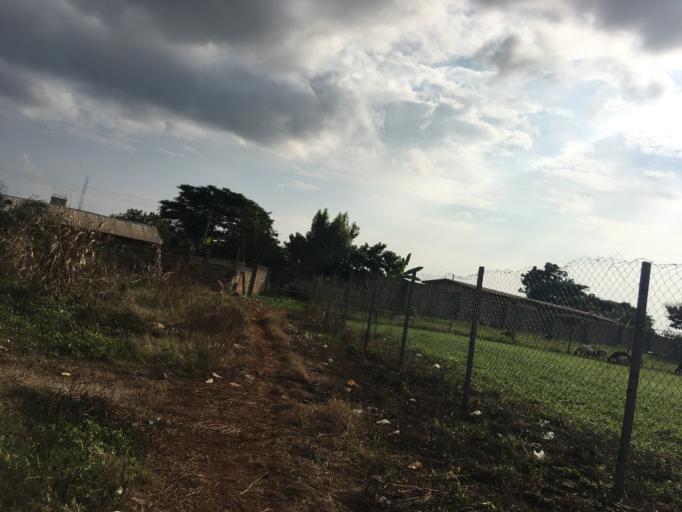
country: GH
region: Western
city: Bibiani
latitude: 6.8063
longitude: -2.5195
